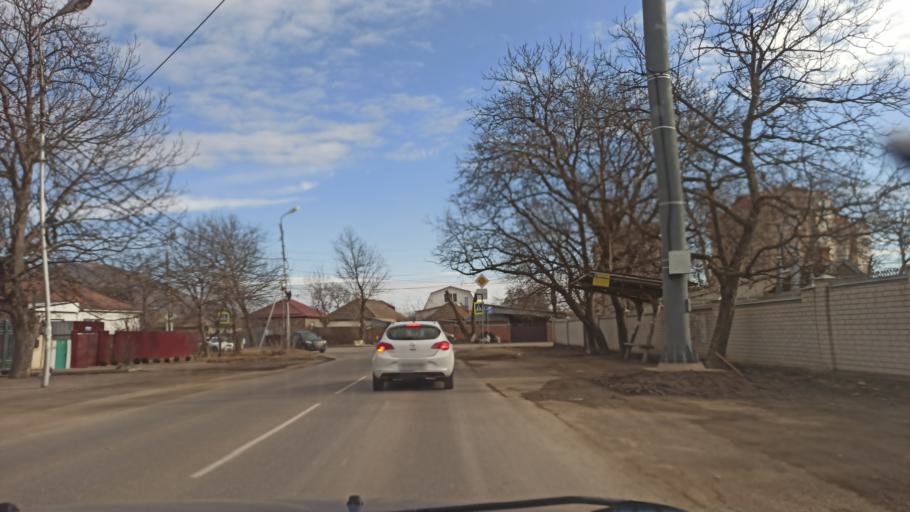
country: RU
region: Stavropol'skiy
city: Svobody
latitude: 44.0326
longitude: 43.0355
